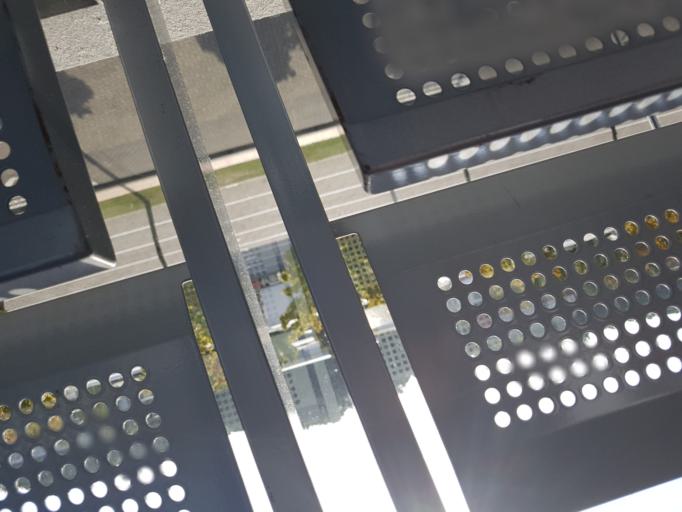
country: DE
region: Schleswig-Holstein
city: Kiel
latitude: 54.3168
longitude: 10.1400
